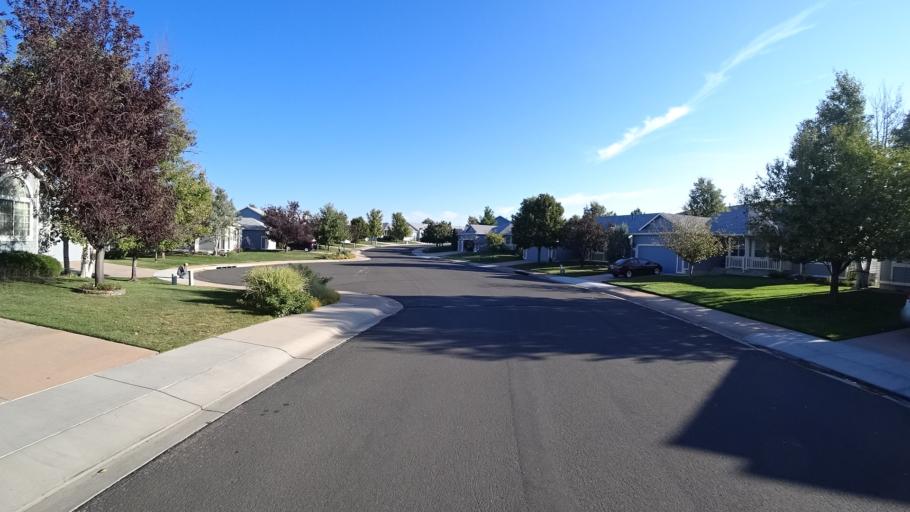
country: US
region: Colorado
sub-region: El Paso County
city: Cimarron Hills
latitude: 38.8909
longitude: -104.7079
